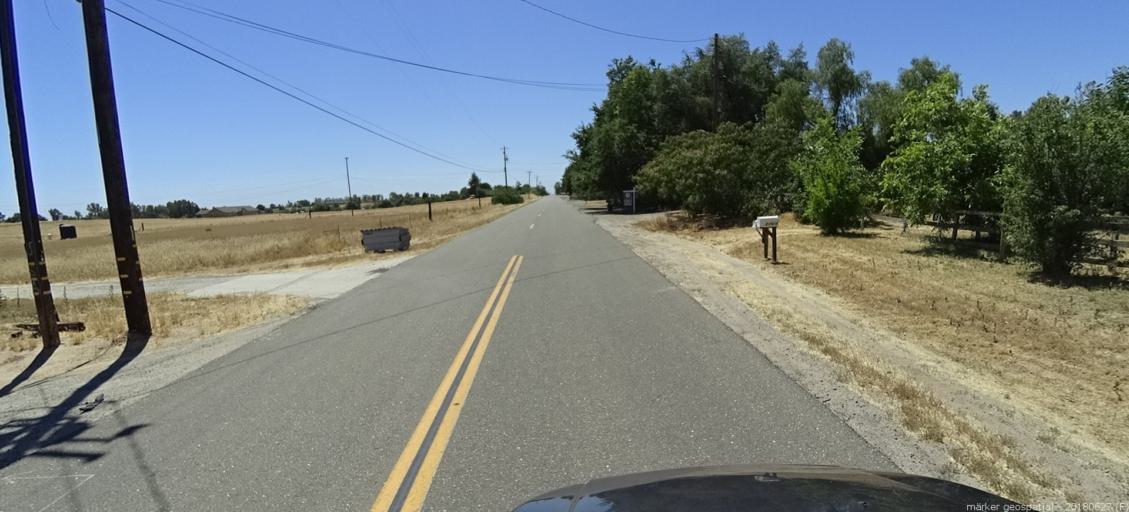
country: US
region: California
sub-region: Madera County
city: Bonadelle Ranchos-Madera Ranchos
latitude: 36.9594
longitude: -119.9039
